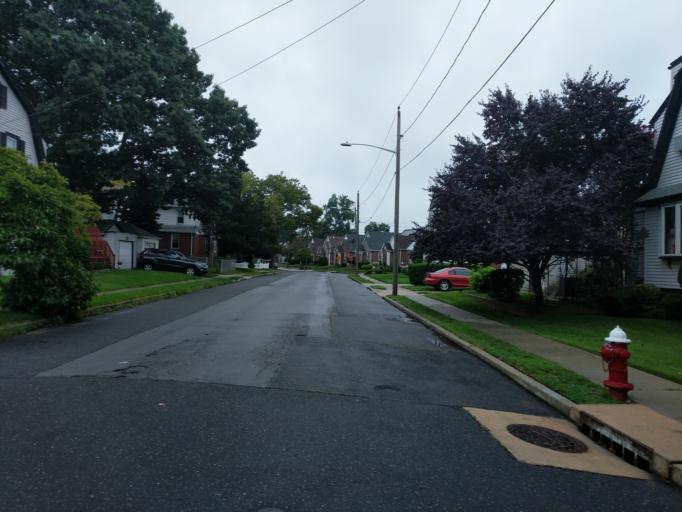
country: US
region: New York
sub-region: Nassau County
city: South Valley Stream
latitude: 40.6519
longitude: -73.7063
